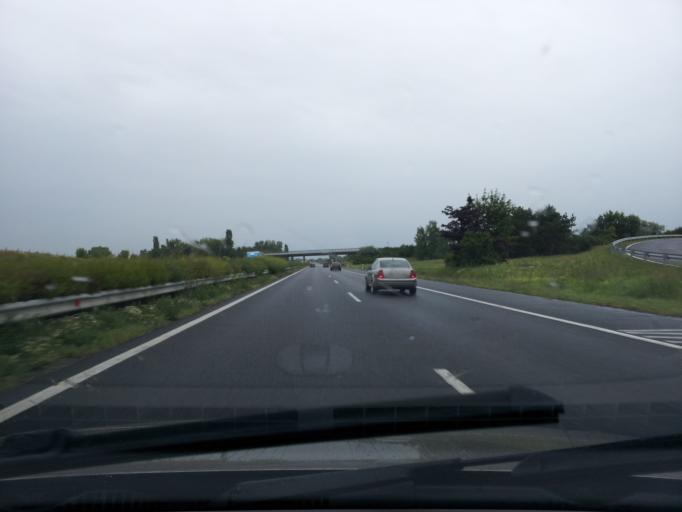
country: HU
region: Fejer
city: Polgardi
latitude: 47.0402
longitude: 18.2920
